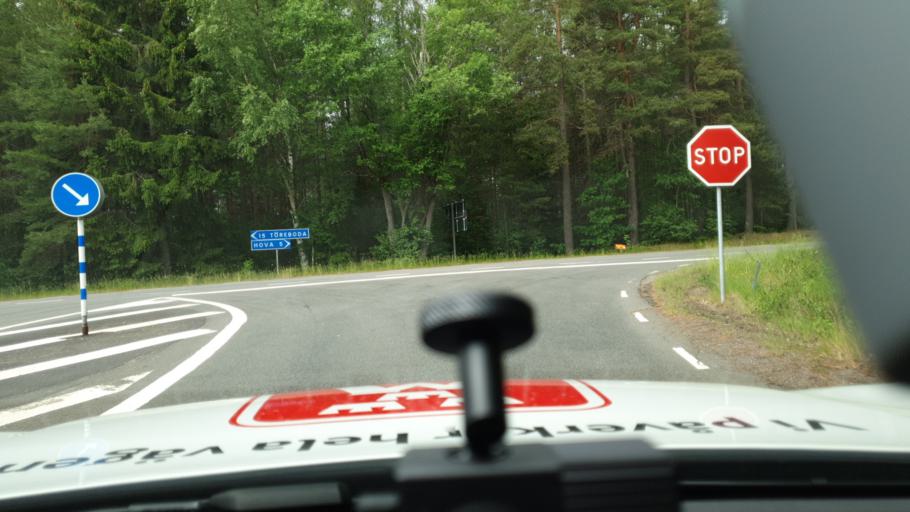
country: SE
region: Vaestra Goetaland
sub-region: Gullspangs Kommun
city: Hova
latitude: 58.8171
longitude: 14.2279
